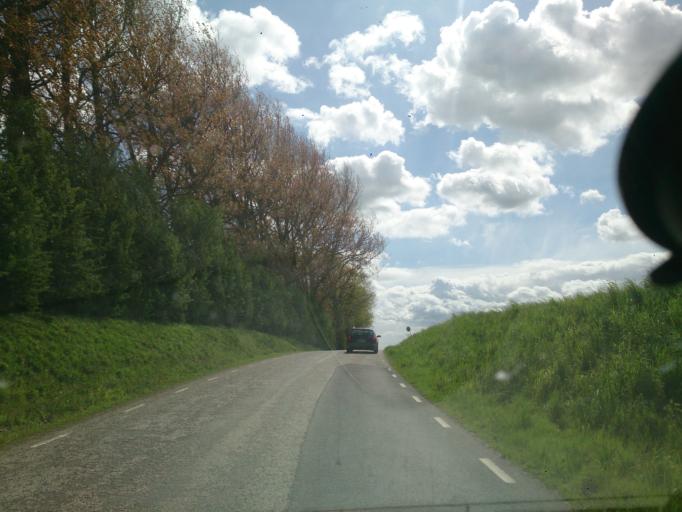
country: SE
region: Skane
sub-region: Ystads Kommun
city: Ystad
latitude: 55.4987
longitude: 13.7098
